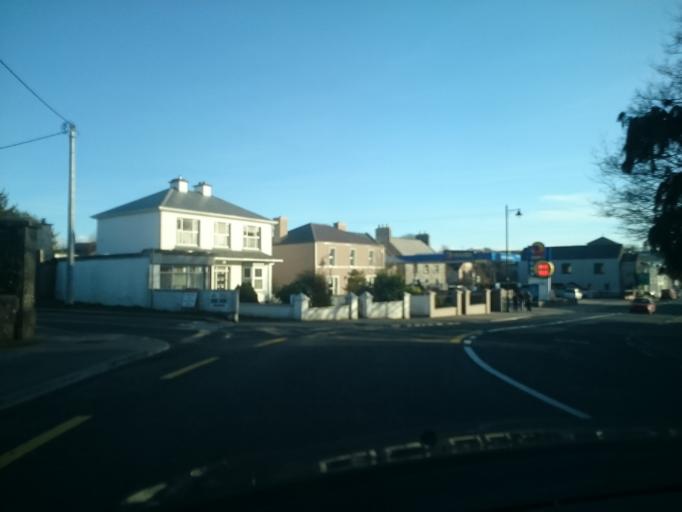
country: IE
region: Connaught
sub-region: Maigh Eo
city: Westport
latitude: 53.8027
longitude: -9.5205
